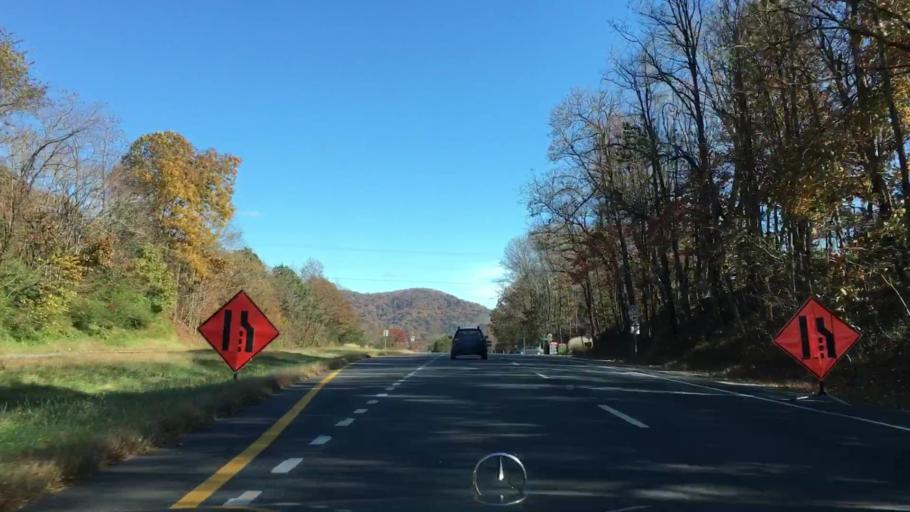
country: US
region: Virginia
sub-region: Albemarle County
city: Crozet
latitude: 37.9680
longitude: -78.6366
